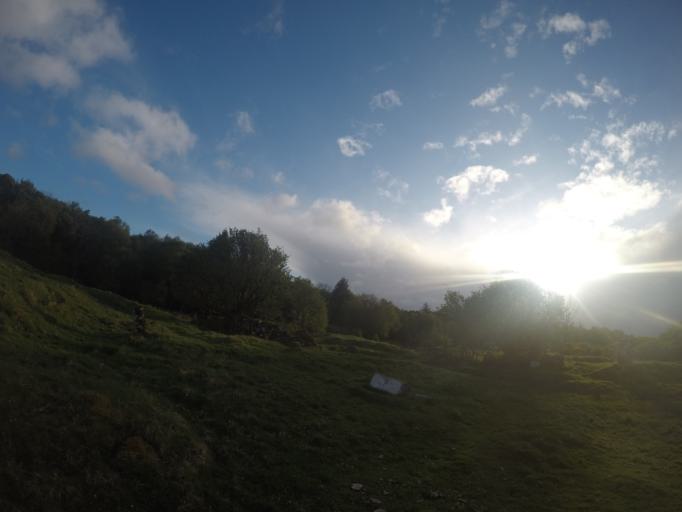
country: GB
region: Scotland
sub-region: Highland
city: Isle of Skye
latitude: 57.4533
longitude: -6.3057
